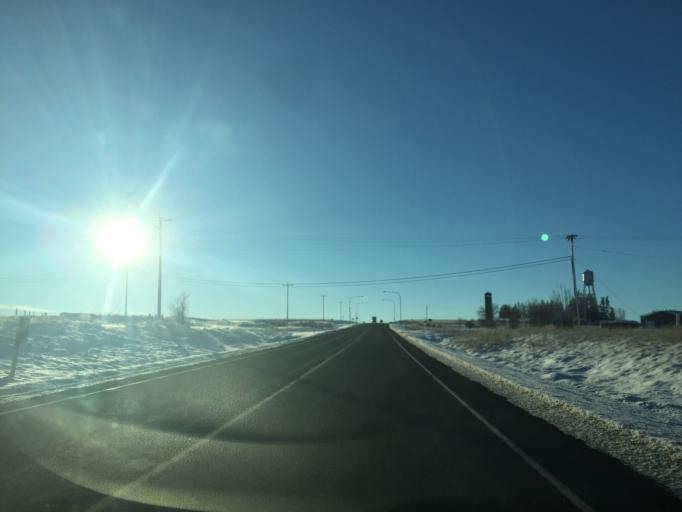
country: US
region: Washington
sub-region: Okanogan County
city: Coulee Dam
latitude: 47.7072
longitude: -118.9357
